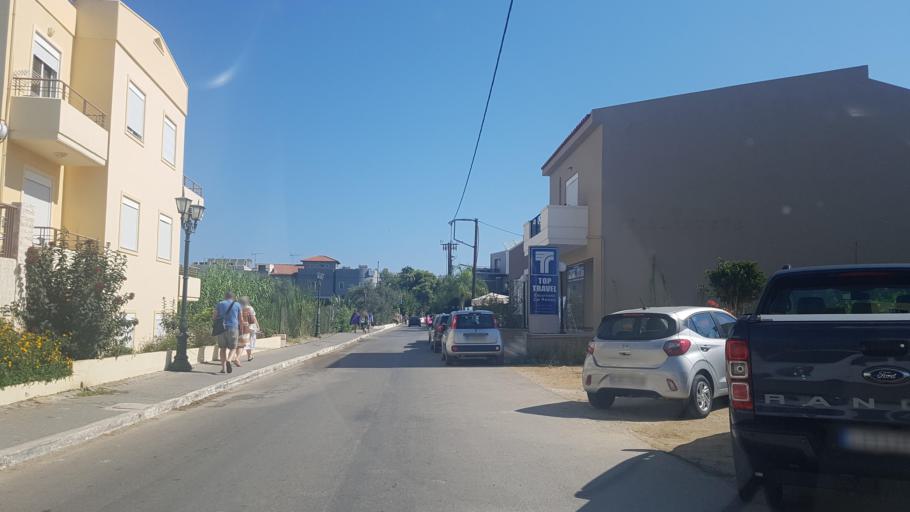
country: GR
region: Crete
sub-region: Nomos Chanias
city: Daratsos
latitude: 35.5106
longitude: 23.9794
